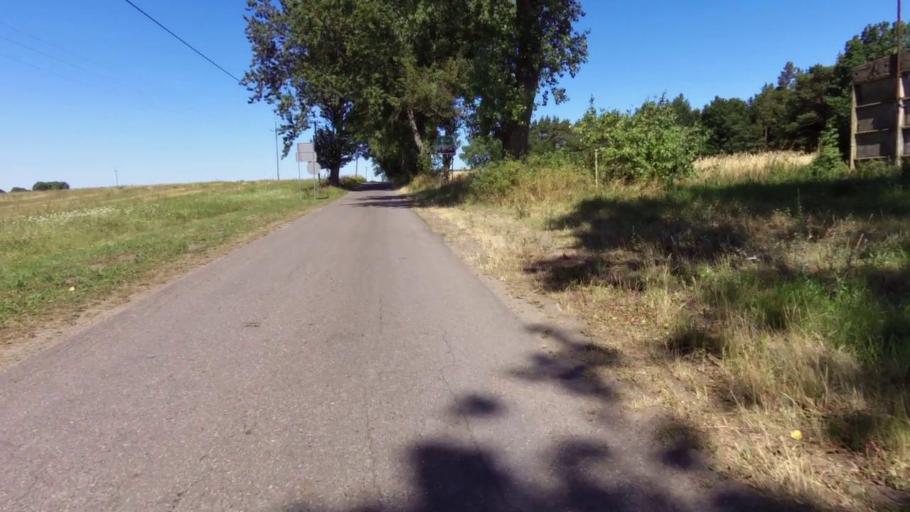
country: PL
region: West Pomeranian Voivodeship
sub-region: Powiat drawski
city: Czaplinek
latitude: 53.5393
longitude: 16.2096
